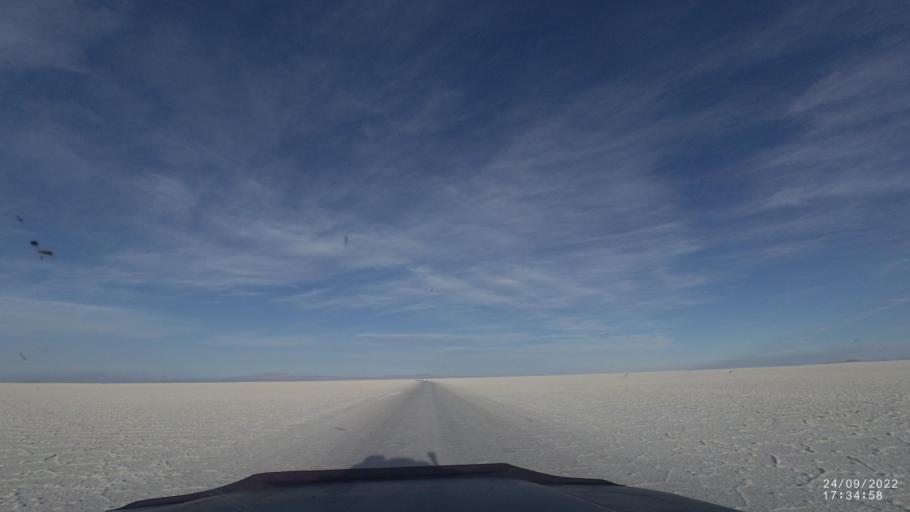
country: BO
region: Potosi
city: Colchani
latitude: -20.3224
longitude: -67.2689
